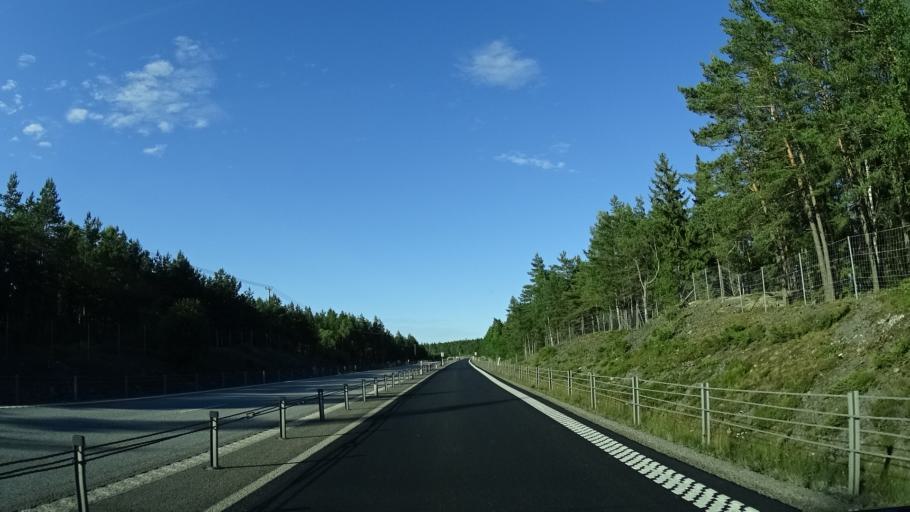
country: SE
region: Stockholm
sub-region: Osterakers Kommun
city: Akersberga
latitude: 59.5875
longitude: 18.2569
